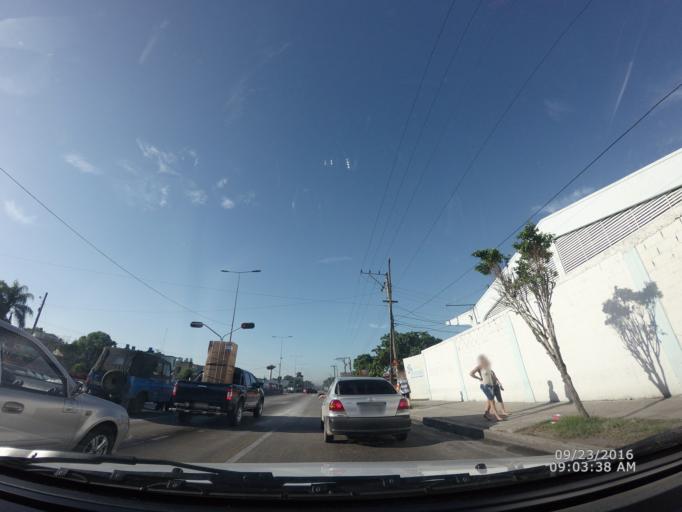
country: CU
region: La Habana
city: Arroyo Naranjo
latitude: 23.0615
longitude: -82.4018
